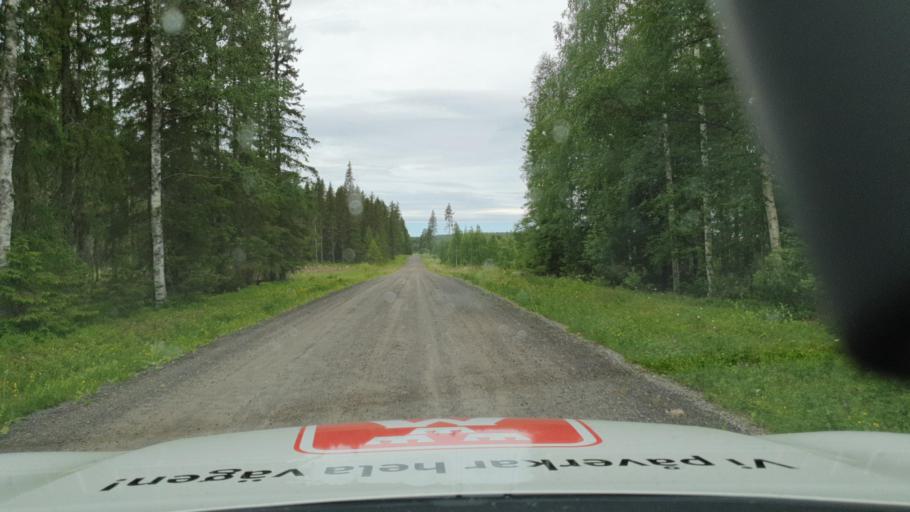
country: SE
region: Vaesterbotten
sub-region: Skelleftea Kommun
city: Burtraesk
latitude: 64.3994
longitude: 20.5647
